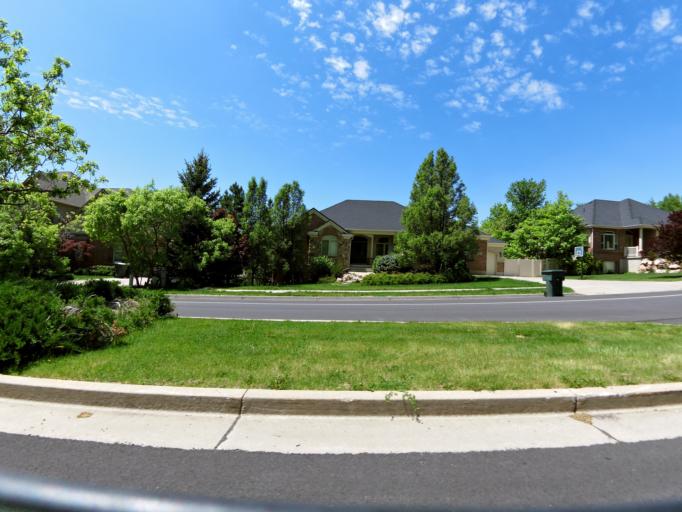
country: US
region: Utah
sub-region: Weber County
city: Uintah
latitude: 41.1647
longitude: -111.9253
